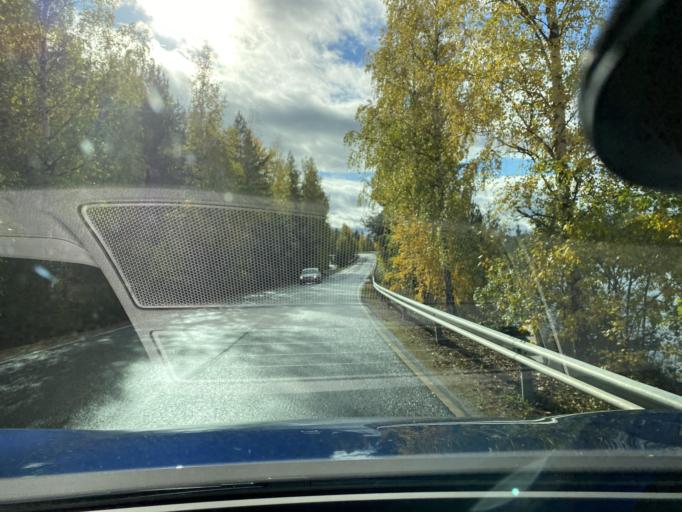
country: FI
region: Pirkanmaa
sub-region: Tampere
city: Nokia
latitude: 61.4800
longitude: 23.3424
